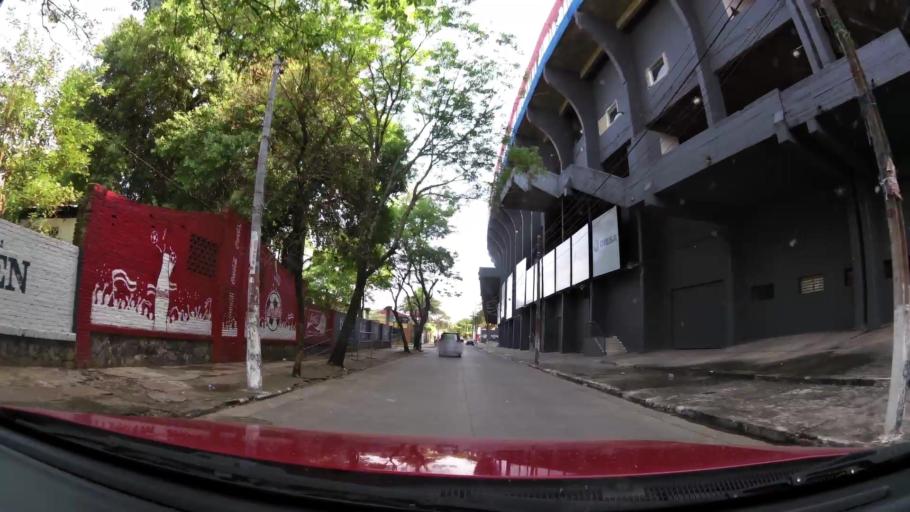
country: PY
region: Asuncion
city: Asuncion
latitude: -25.2923
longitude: -57.6584
